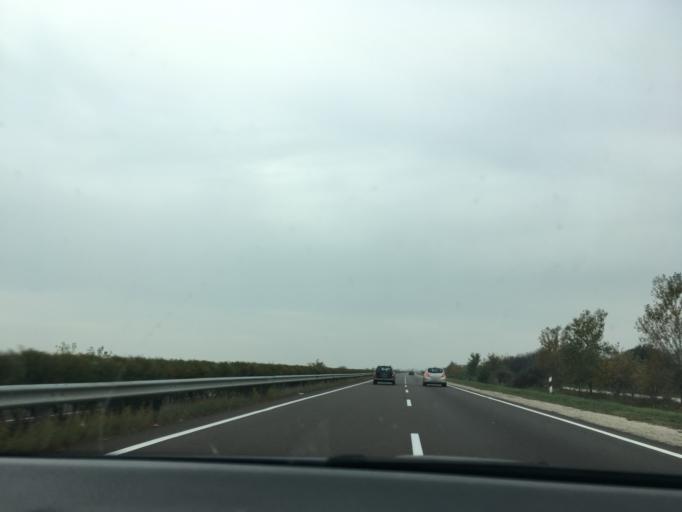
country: HU
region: Pest
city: Cegled
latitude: 47.1908
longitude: 19.8730
